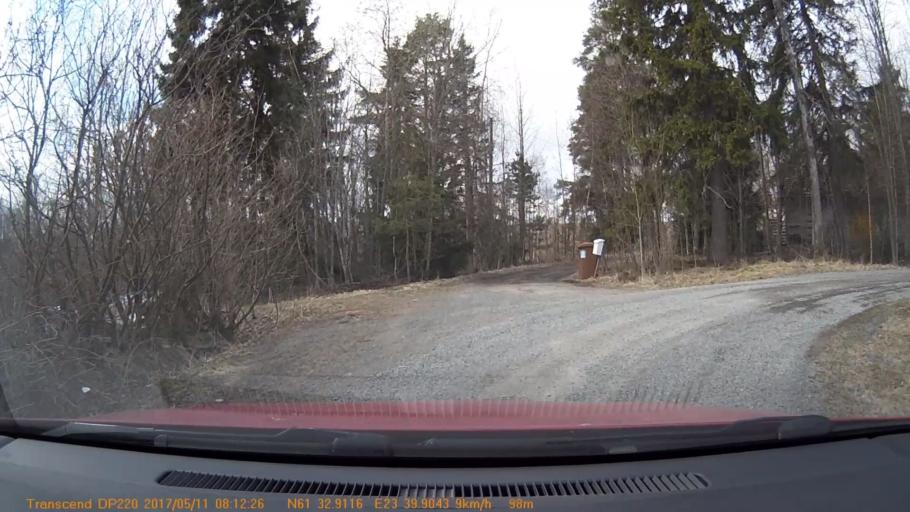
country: FI
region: Pirkanmaa
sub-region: Tampere
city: Yloejaervi
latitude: 61.5486
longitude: 23.6651
